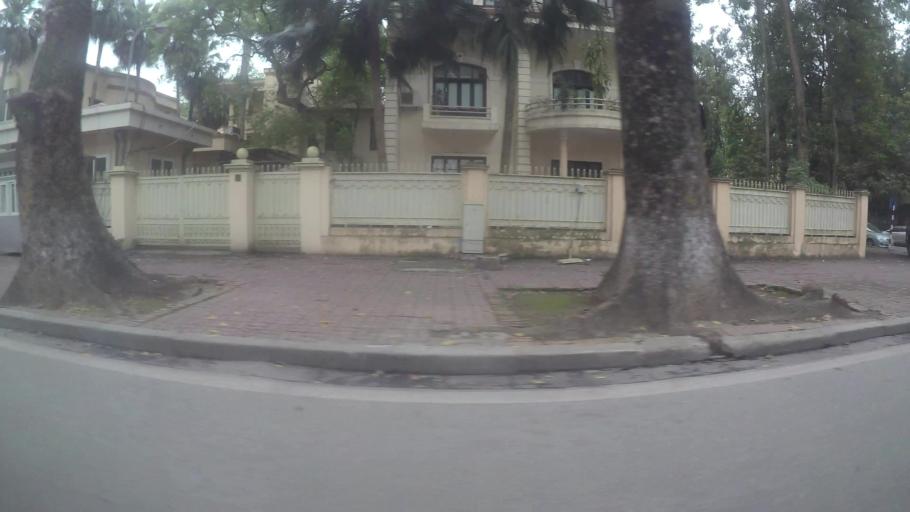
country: VN
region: Ha Noi
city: Hanoi
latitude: 21.0339
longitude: 105.8354
